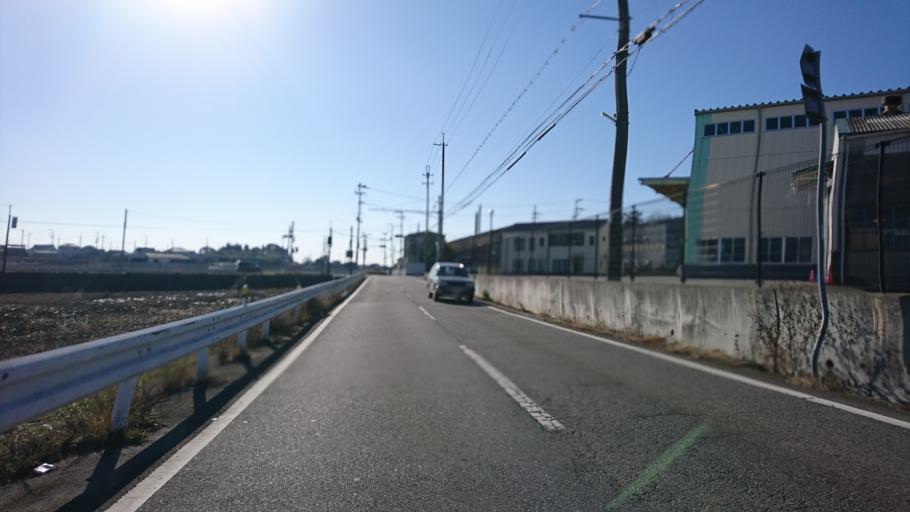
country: JP
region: Hyogo
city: Miki
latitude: 34.7526
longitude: 134.9258
